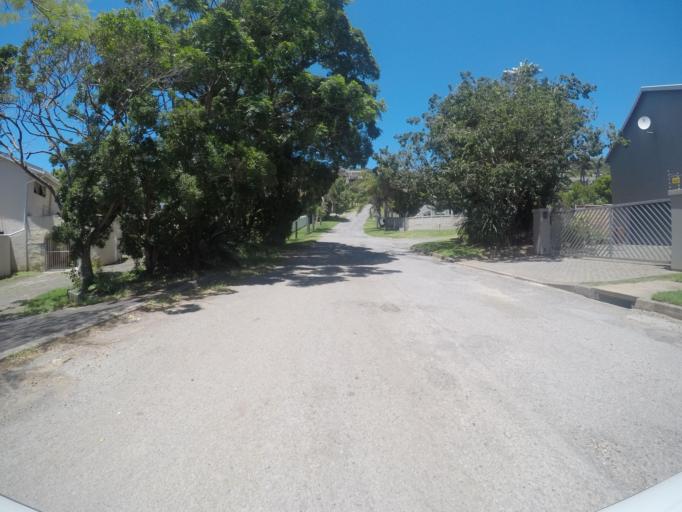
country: ZA
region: Eastern Cape
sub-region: Buffalo City Metropolitan Municipality
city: East London
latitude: -32.9348
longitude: 28.0116
